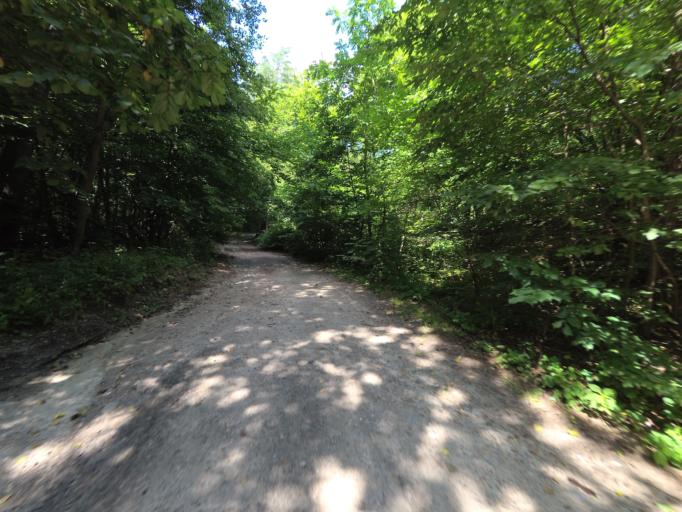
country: PL
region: Pomeranian Voivodeship
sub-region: Gdynia
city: Wielki Kack
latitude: 54.4885
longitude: 18.5019
